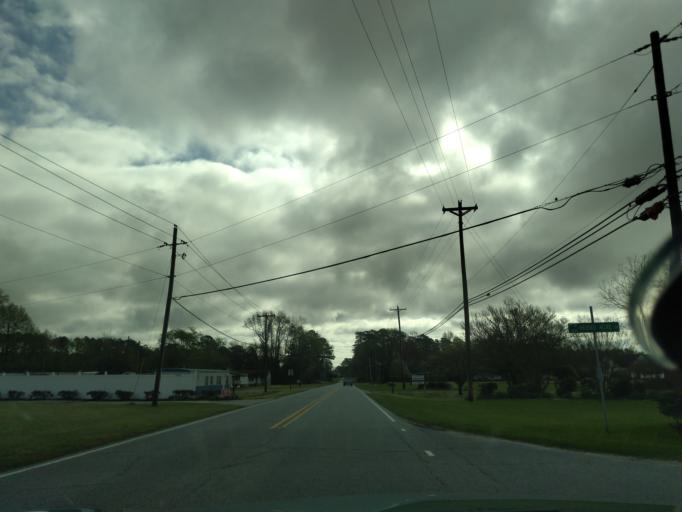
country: US
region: North Carolina
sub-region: Chowan County
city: Edenton
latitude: 36.0575
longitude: -76.6631
